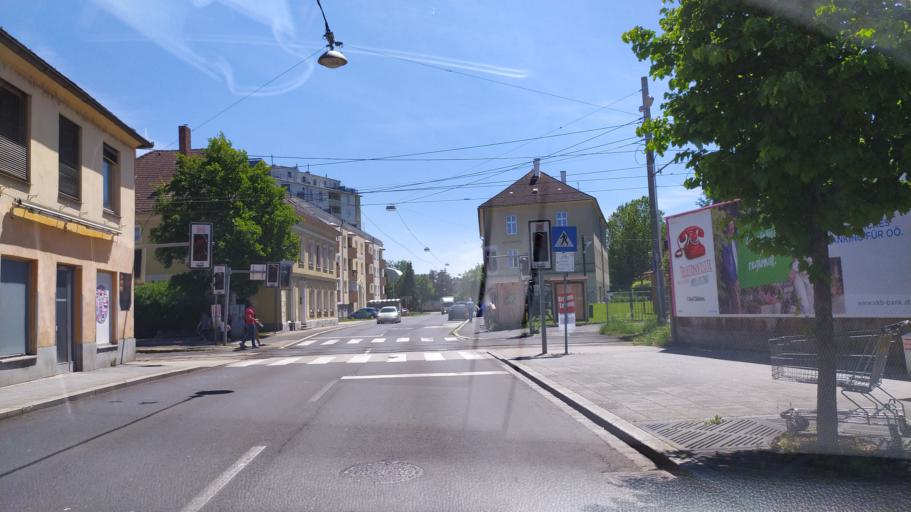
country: AT
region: Upper Austria
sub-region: Politischer Bezirk Linz-Land
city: Ansfelden
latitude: 48.2529
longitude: 14.3137
